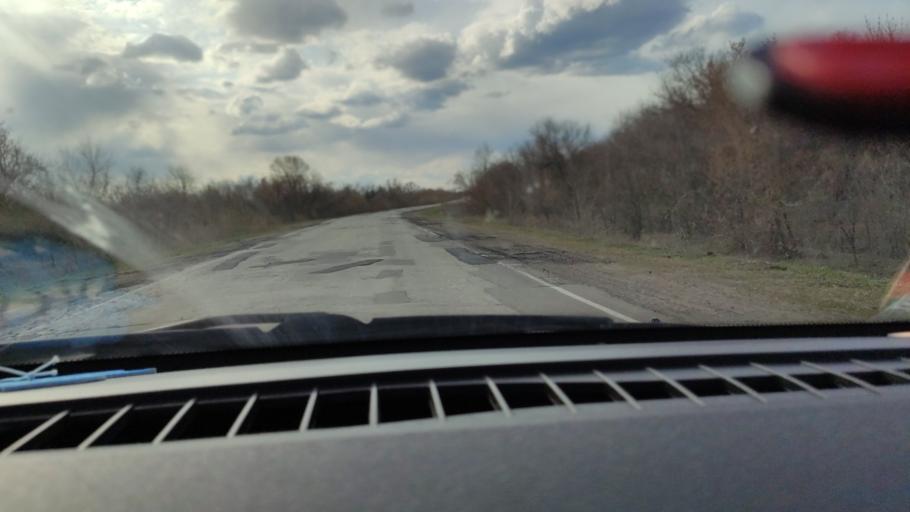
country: RU
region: Saratov
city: Krasnoarmeysk
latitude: 51.0734
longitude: 45.9821
